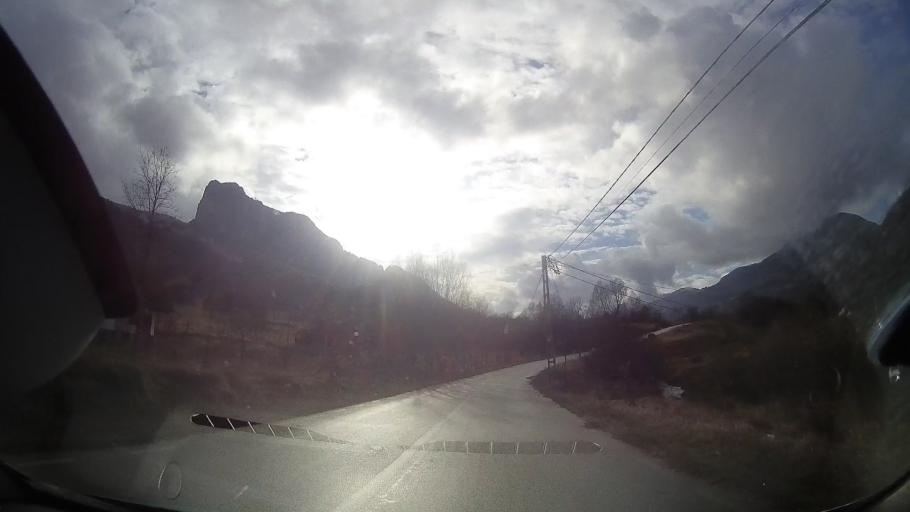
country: RO
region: Alba
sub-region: Comuna Rimetea
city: Rimetea
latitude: 46.4706
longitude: 23.5830
